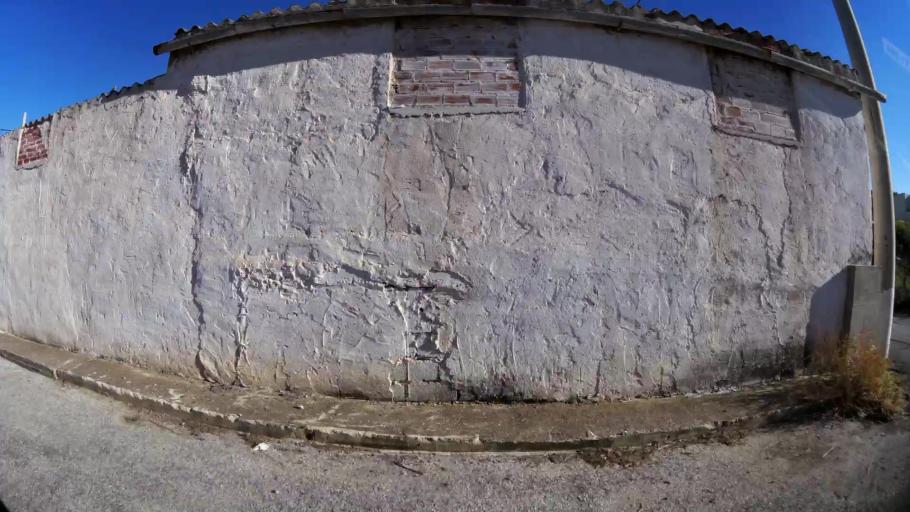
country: GR
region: Attica
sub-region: Nomarchia Anatolikis Attikis
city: Koropi
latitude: 37.8940
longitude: 23.8648
